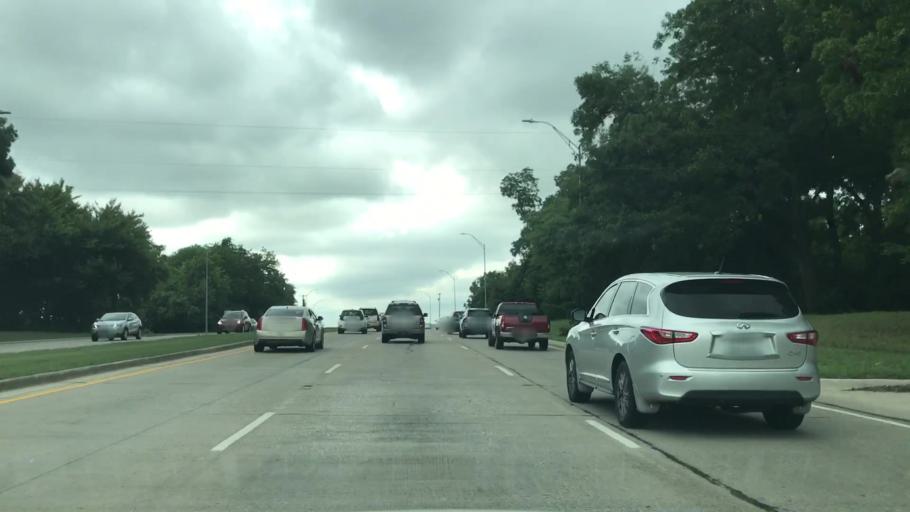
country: US
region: Texas
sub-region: Dallas County
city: Rowlett
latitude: 32.9104
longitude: -96.6009
